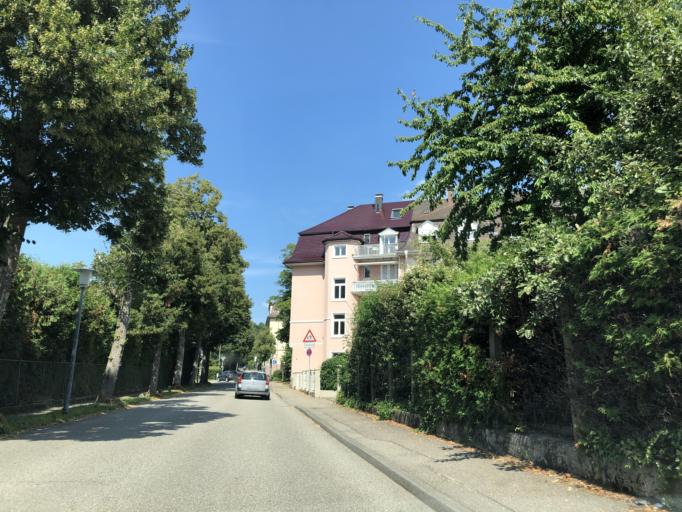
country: DE
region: Baden-Wuerttemberg
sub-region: Karlsruhe Region
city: Baden-Baden
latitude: 48.7460
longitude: 8.2572
